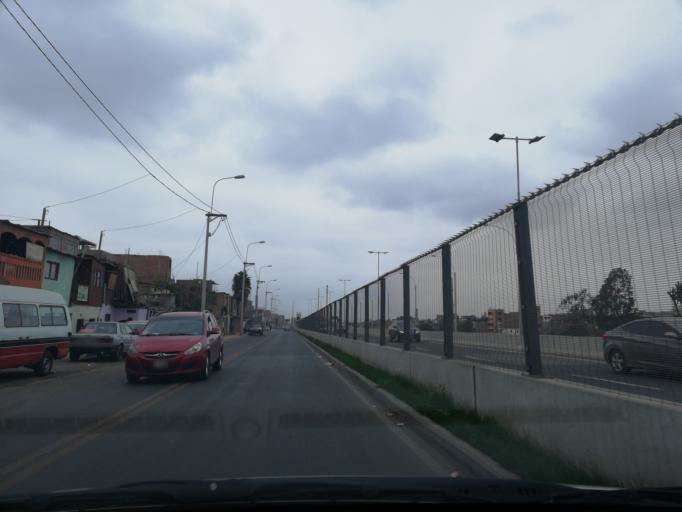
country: PE
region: Lima
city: Lima
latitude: -12.0357
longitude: -77.0621
